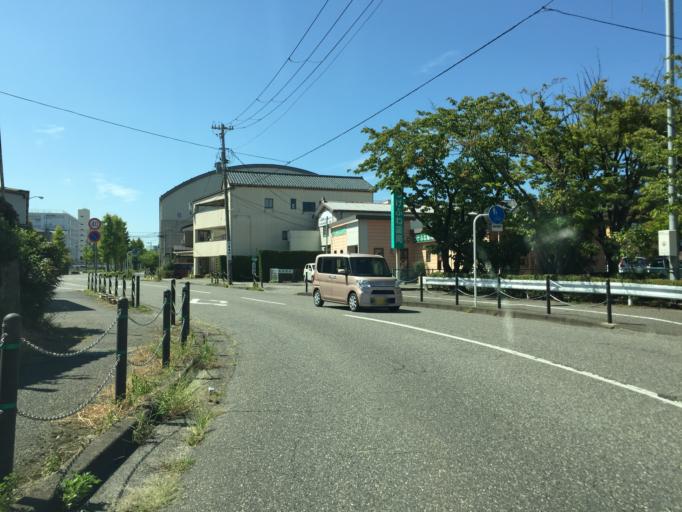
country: JP
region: Niigata
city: Niigata-shi
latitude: 37.9349
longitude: 139.0567
